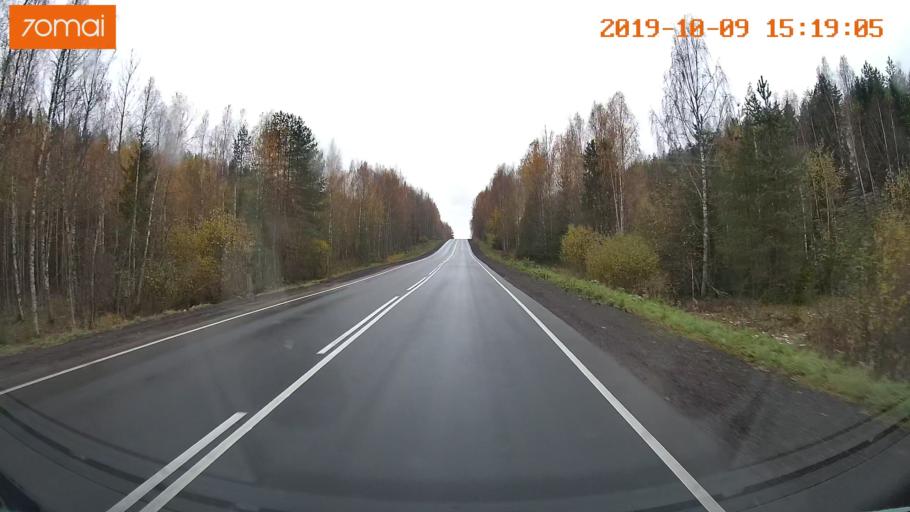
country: RU
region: Kostroma
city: Susanino
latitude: 58.0794
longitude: 41.5625
